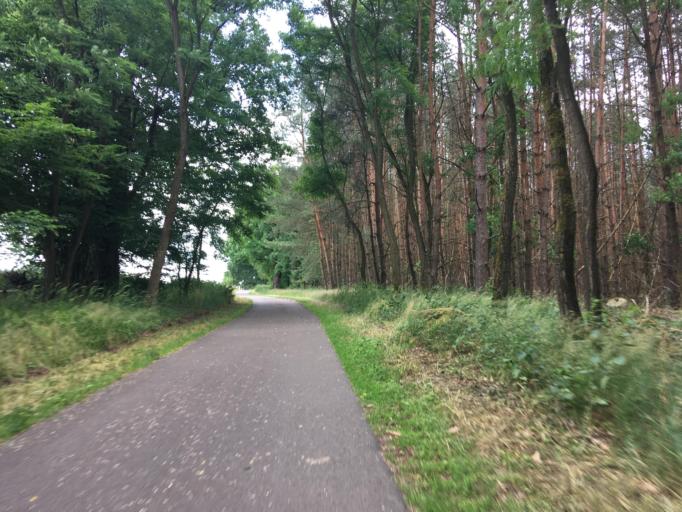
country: DE
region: Brandenburg
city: Althuttendorf
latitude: 53.0247
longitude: 13.8548
